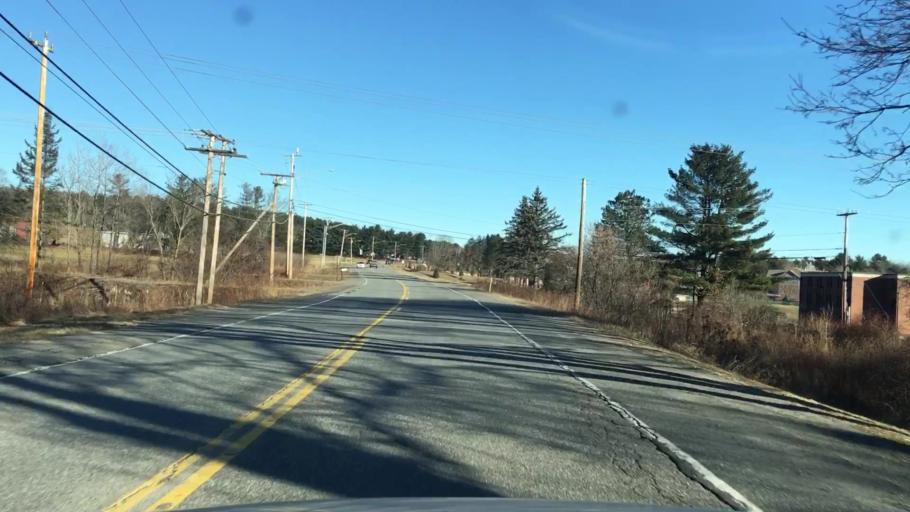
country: US
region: Maine
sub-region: Kennebec County
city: Waterville
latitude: 44.5231
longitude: -69.6669
